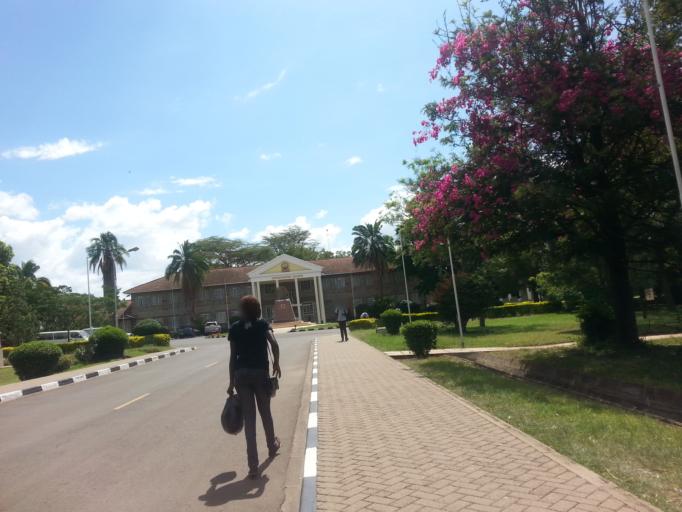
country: KE
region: Nakuru
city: Rongai
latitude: -0.1664
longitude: 35.9667
